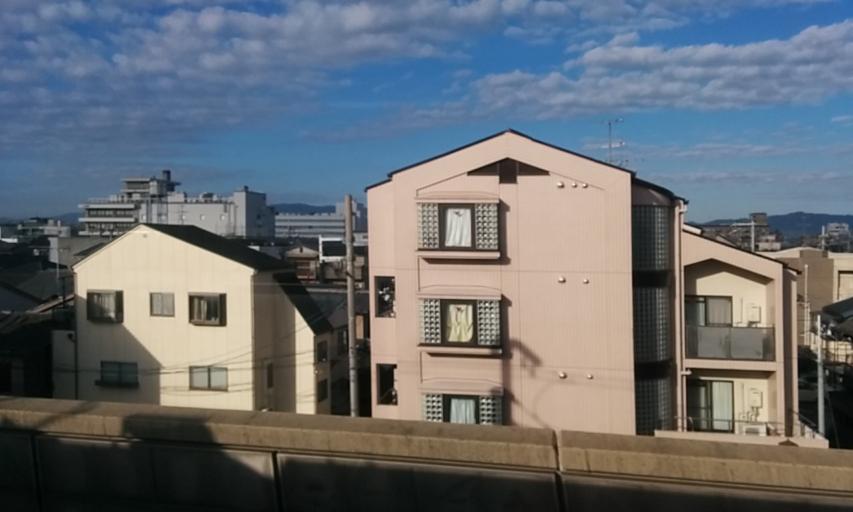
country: JP
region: Kyoto
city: Kyoto
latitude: 34.9774
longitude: 135.7525
